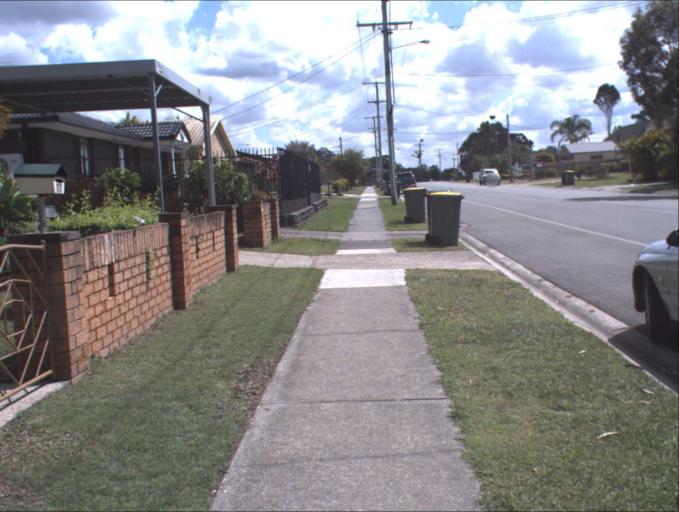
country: AU
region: Queensland
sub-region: Logan
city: Waterford West
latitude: -27.6863
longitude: 153.1548
